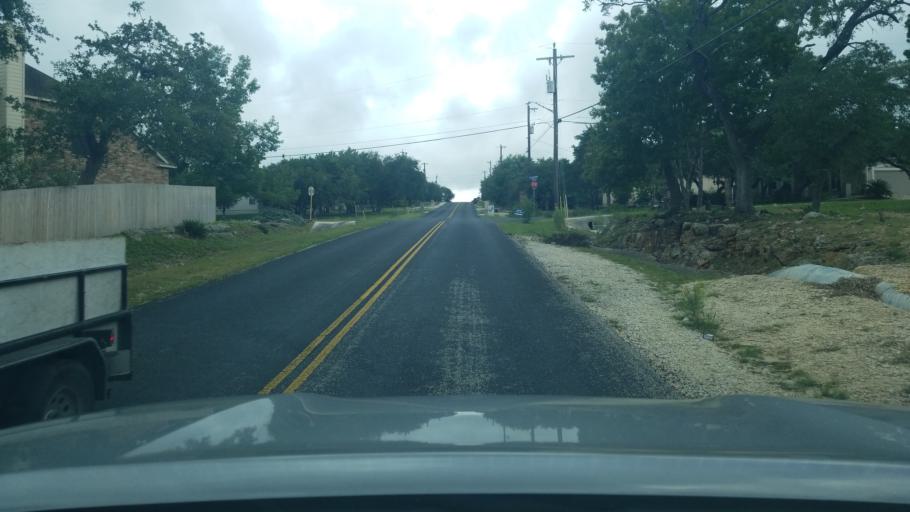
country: US
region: Texas
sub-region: Bexar County
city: Timberwood Park
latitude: 29.6924
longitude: -98.5078
